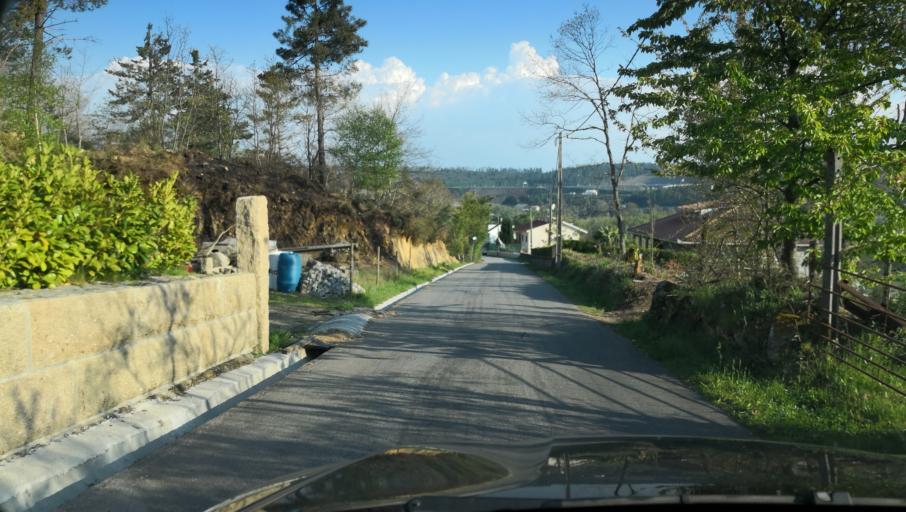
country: PT
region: Vila Real
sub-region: Santa Marta de Penaguiao
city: Santa Marta de Penaguiao
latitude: 41.2905
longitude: -7.8361
